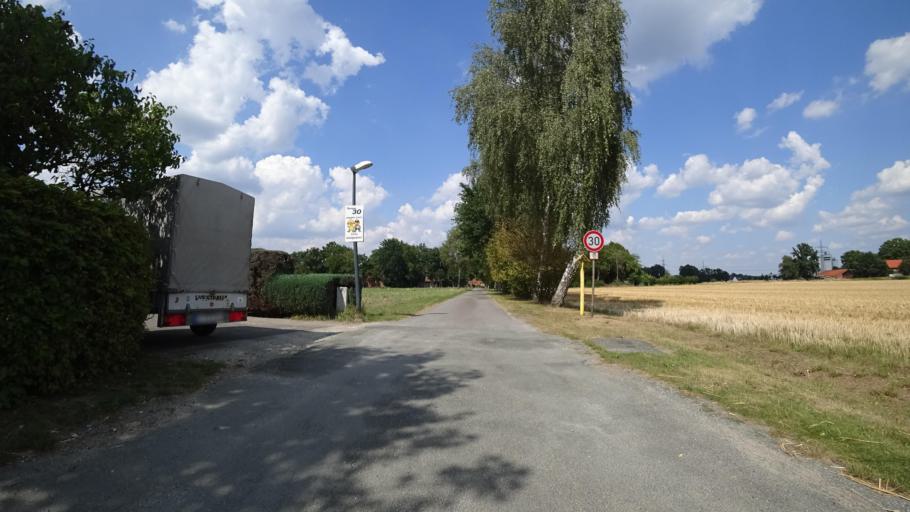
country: DE
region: North Rhine-Westphalia
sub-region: Regierungsbezirk Detmold
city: Guetersloh
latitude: 51.9201
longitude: 8.4173
